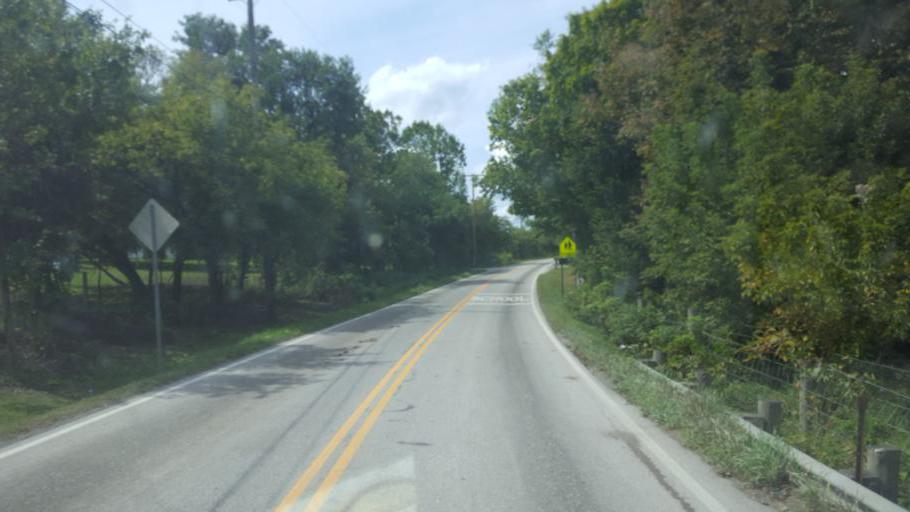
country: US
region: Ohio
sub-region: Geauga County
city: Middlefield
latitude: 41.4205
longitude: -81.0068
